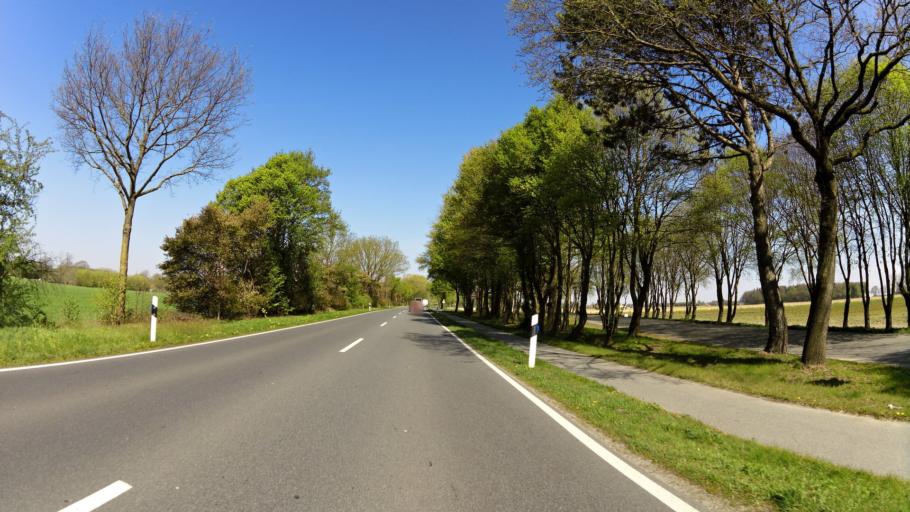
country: DE
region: Lower Saxony
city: Ganderkesee
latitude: 53.0714
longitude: 8.5275
